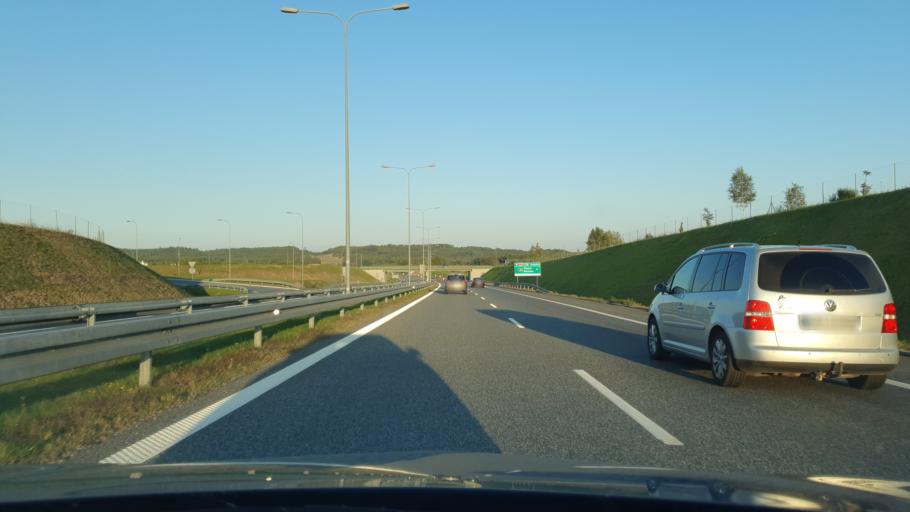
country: PL
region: Pomeranian Voivodeship
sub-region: Powiat slupski
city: Kobylnica
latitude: 54.4250
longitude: 17.0016
